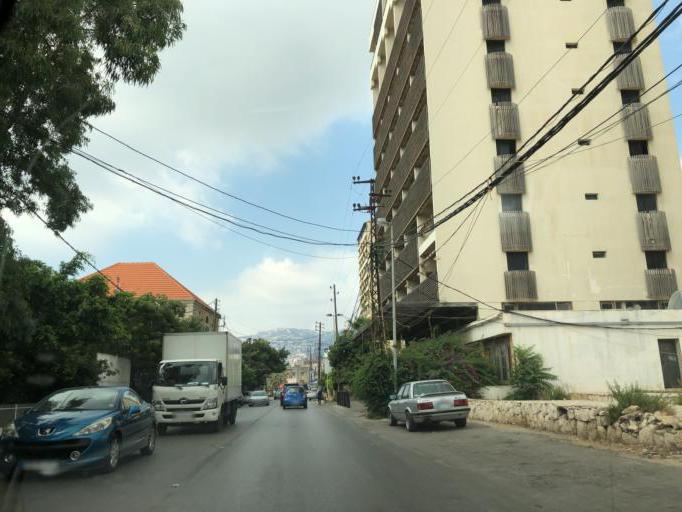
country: LB
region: Mont-Liban
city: Djounie
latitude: 33.9912
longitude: 35.6391
